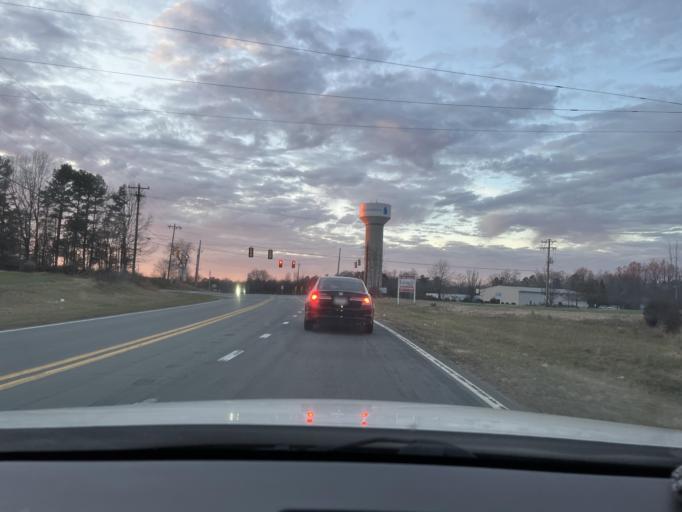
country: US
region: North Carolina
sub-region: Guilford County
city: McLeansville
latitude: 36.0788
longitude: -79.6393
